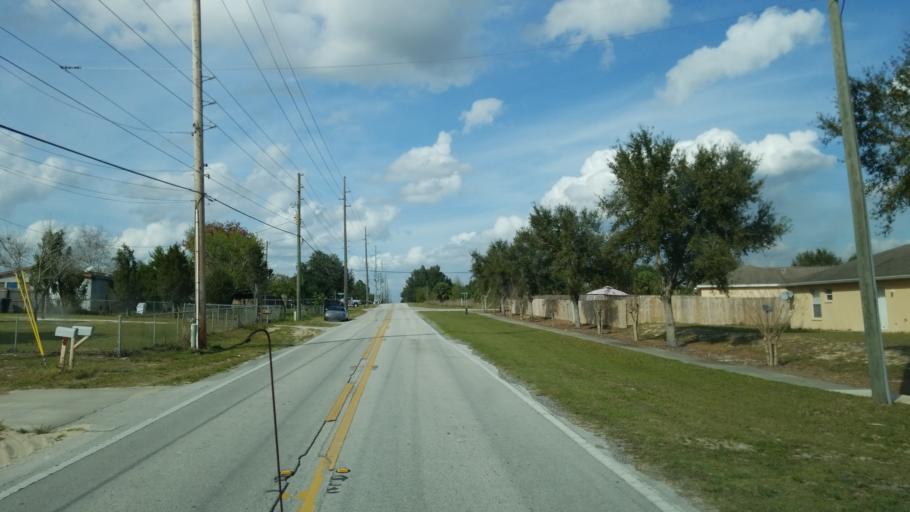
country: US
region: Florida
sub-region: Polk County
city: Davenport
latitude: 28.1418
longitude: -81.5903
